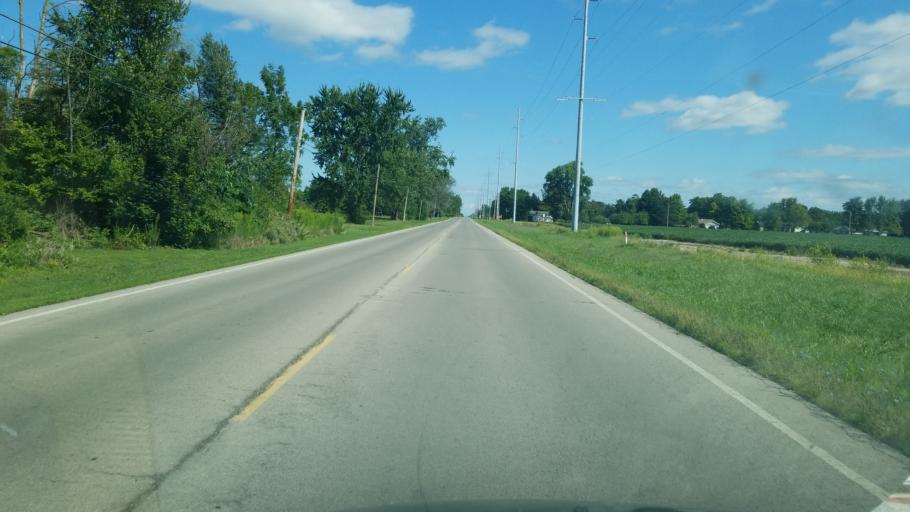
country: US
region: Ohio
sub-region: Hancock County
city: Findlay
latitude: 41.1133
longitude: -83.6496
